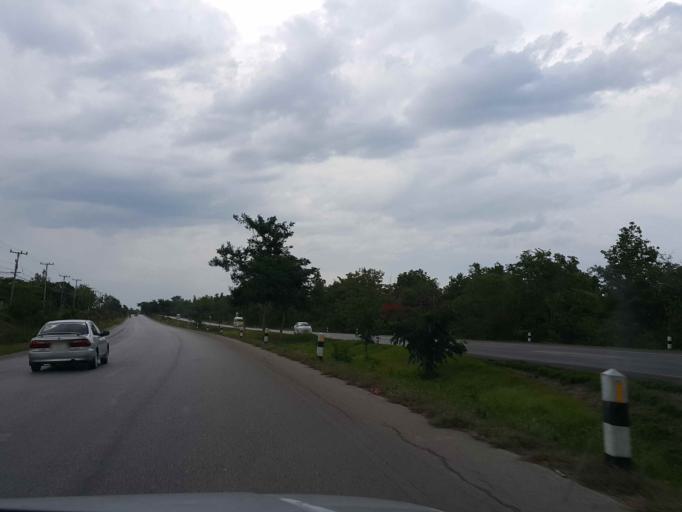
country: TH
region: Lampang
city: Sop Prap
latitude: 17.9894
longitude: 99.3569
